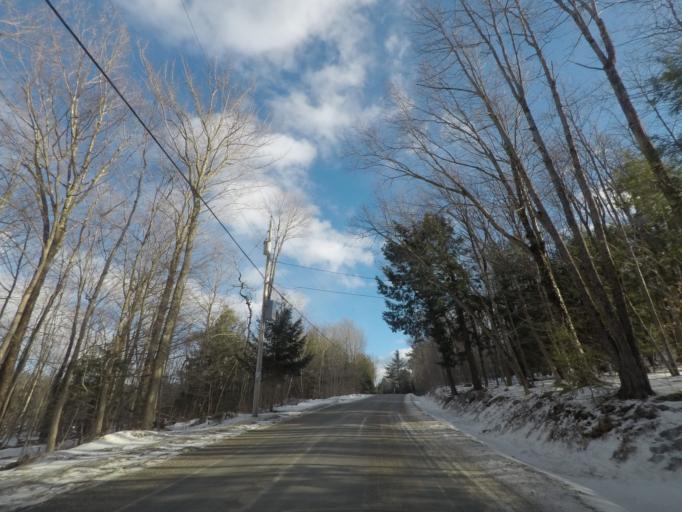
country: US
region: New York
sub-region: Rensselaer County
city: Poestenkill
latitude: 42.7521
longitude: -73.4857
